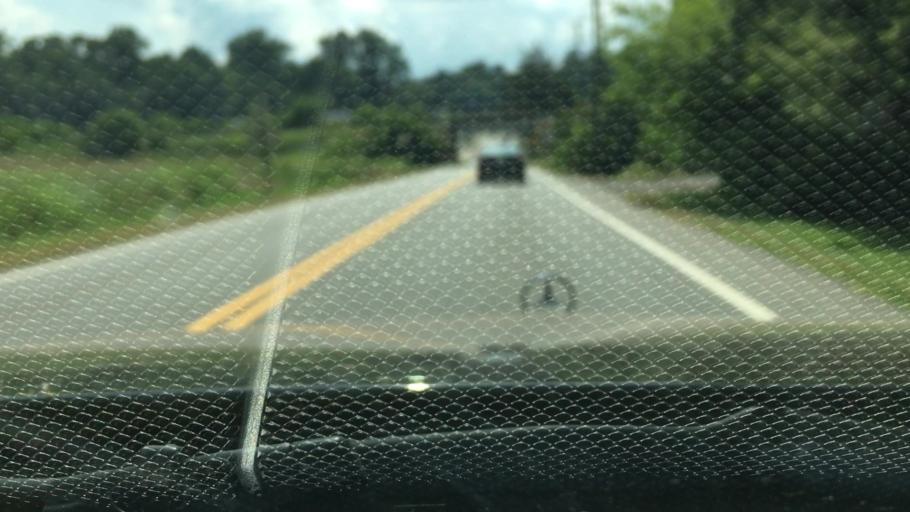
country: US
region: Virginia
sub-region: Orange County
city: Orange
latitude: 38.2406
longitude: -78.1073
